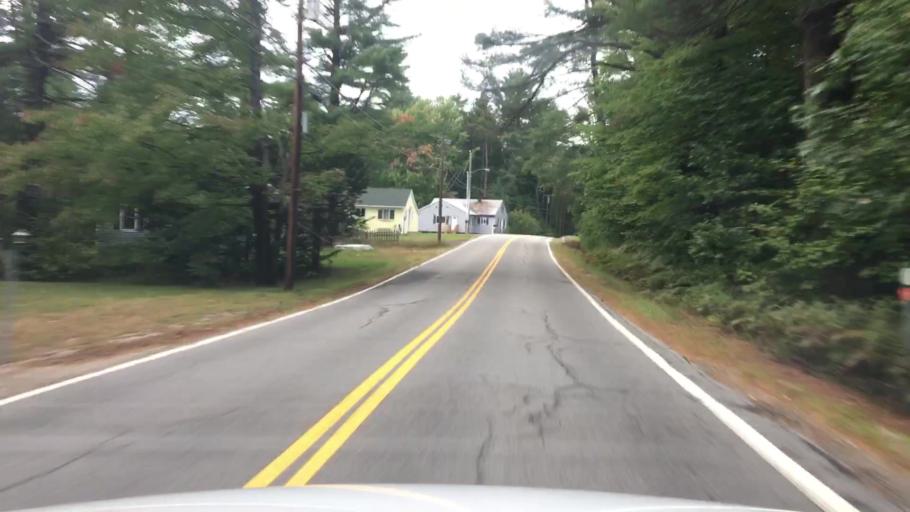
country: US
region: New Hampshire
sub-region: Carroll County
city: Effingham
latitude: 43.7231
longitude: -70.9995
